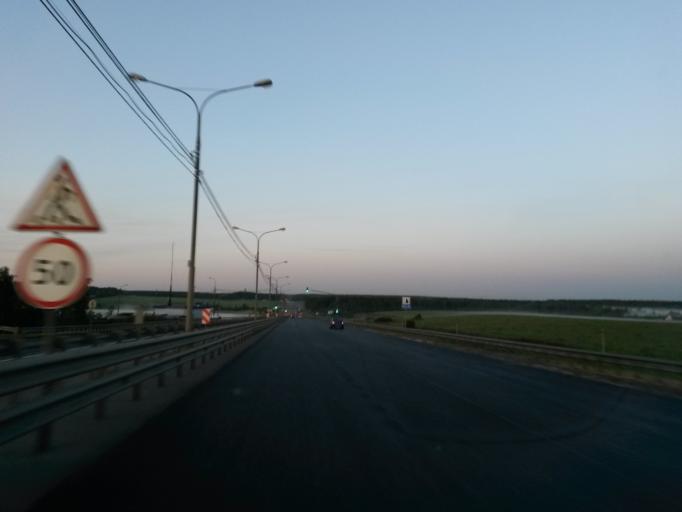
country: RU
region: Moskovskaya
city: Svatkovo
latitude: 56.3367
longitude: 38.2604
